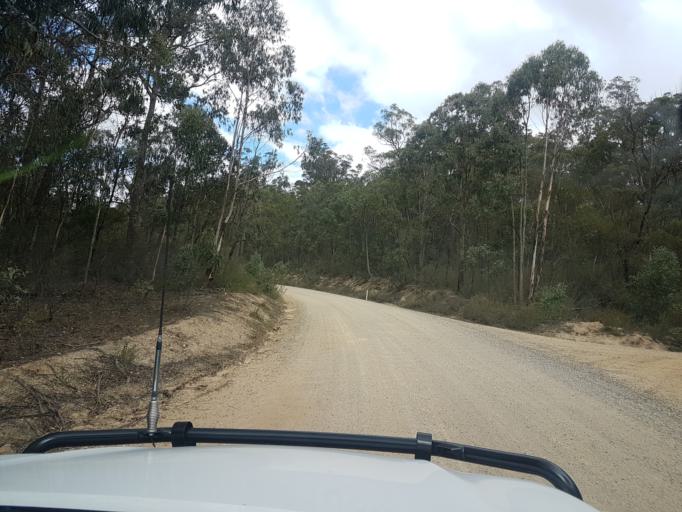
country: AU
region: Victoria
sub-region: East Gippsland
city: Bairnsdale
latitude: -37.6789
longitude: 147.5510
